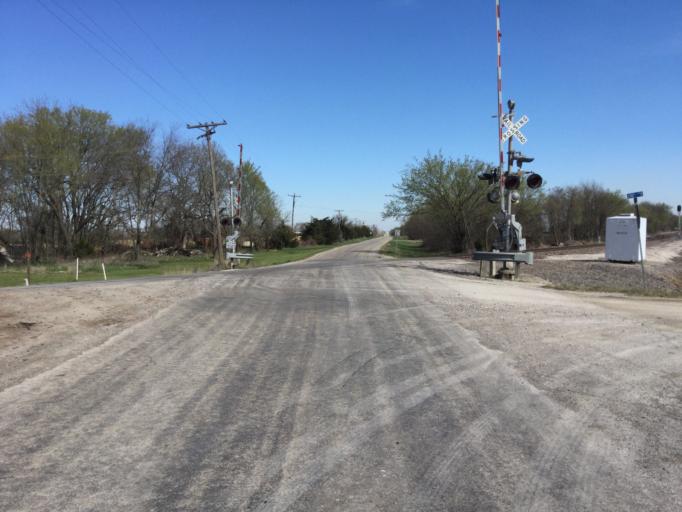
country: US
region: Kansas
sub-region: Neosho County
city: Erie
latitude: 37.6609
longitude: -95.1611
